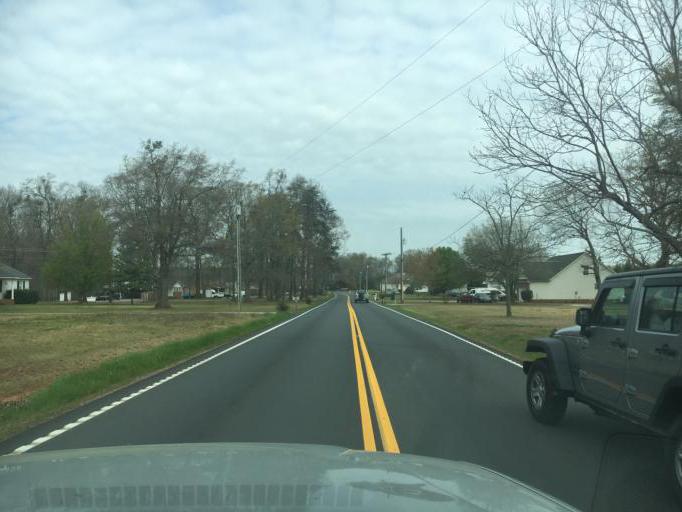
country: US
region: South Carolina
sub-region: Spartanburg County
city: Inman
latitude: 35.0091
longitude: -82.0742
